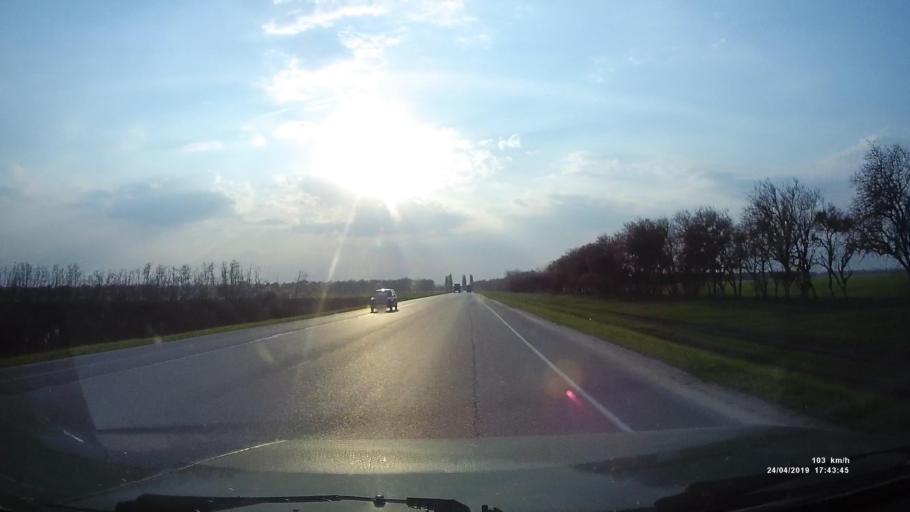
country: RU
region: Rostov
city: Tselina
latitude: 46.5354
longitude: 40.9199
